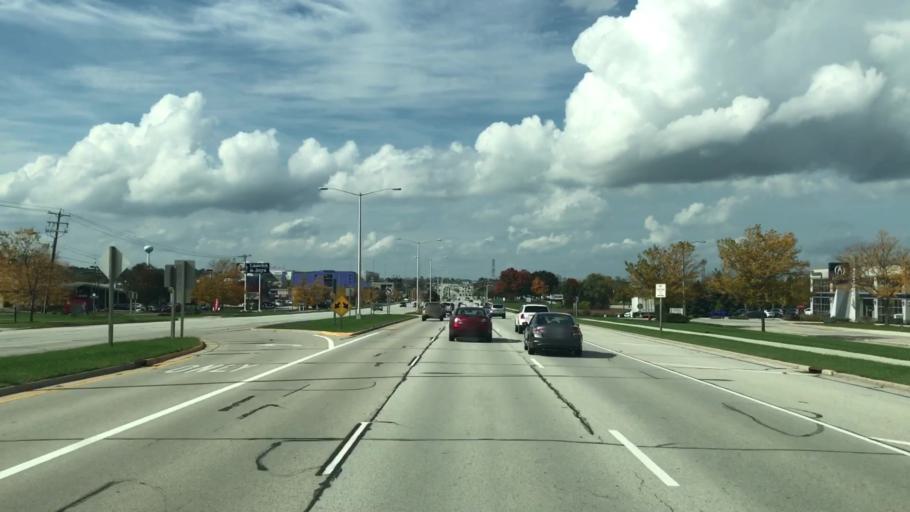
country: US
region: Wisconsin
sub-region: Waukesha County
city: Brookfield
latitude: 43.0361
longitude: -88.1498
